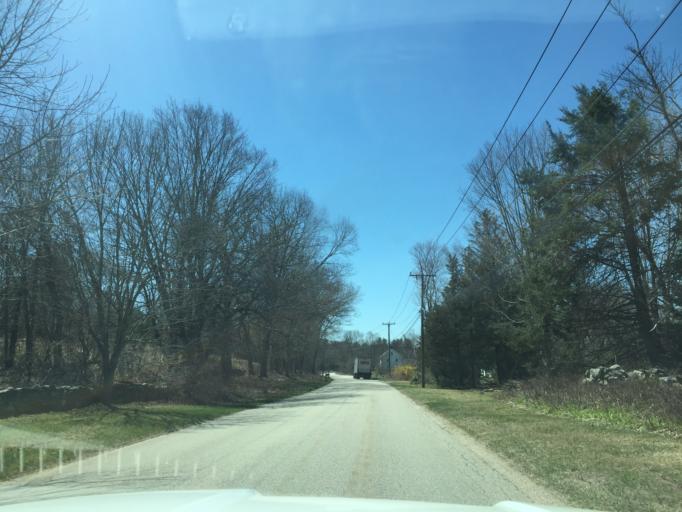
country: US
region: Connecticut
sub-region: Windham County
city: Quinebaug
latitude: 41.9865
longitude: -71.9523
